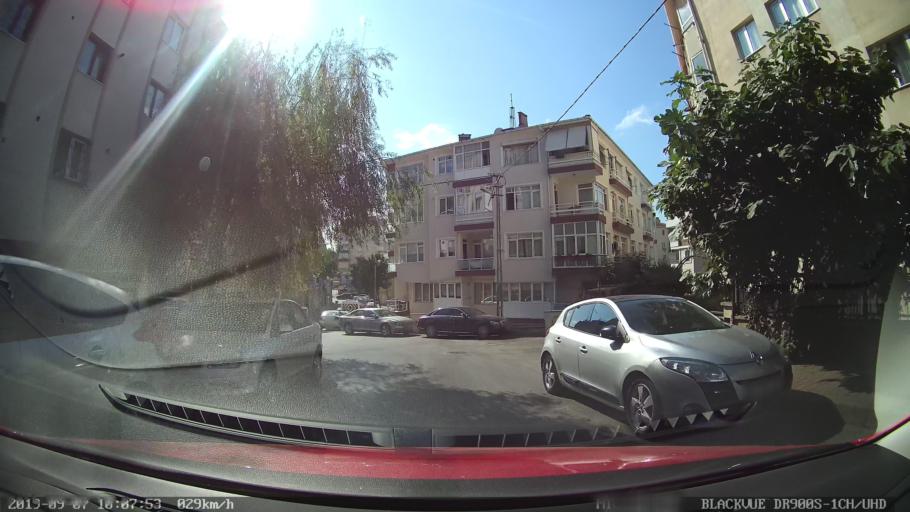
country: TR
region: Istanbul
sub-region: Atasehir
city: Atasehir
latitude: 40.9486
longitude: 29.1127
